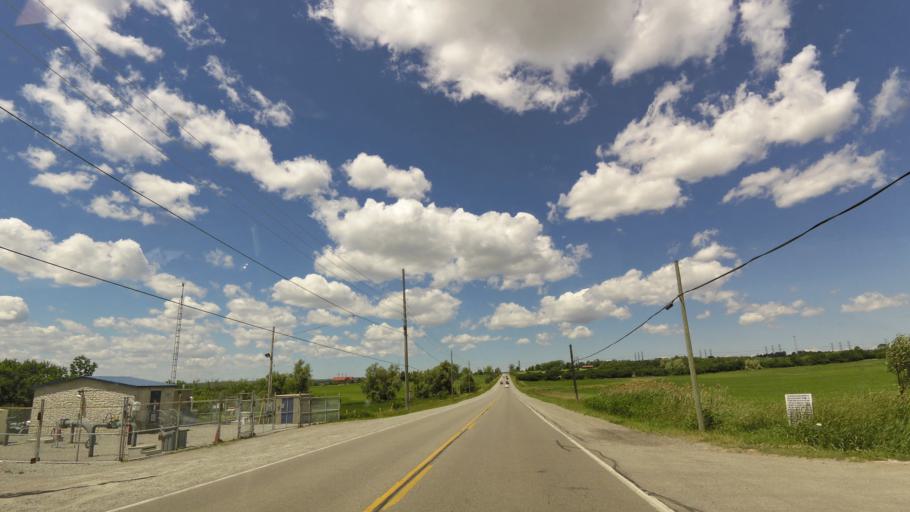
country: CA
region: Ontario
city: Oshawa
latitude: 43.9637
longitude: -78.8602
